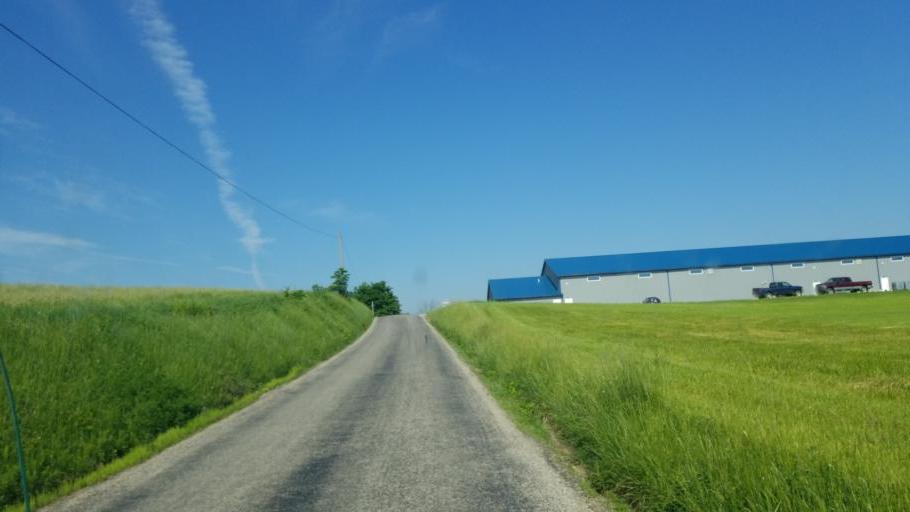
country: US
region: Ohio
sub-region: Holmes County
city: Millersburg
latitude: 40.5211
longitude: -81.8369
